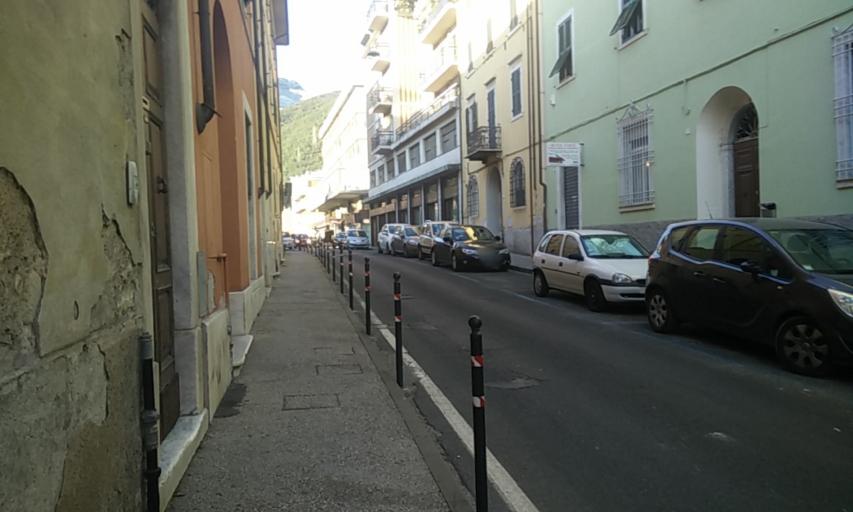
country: IT
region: Tuscany
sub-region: Provincia di Massa-Carrara
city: Carrara
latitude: 44.0761
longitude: 10.0961
